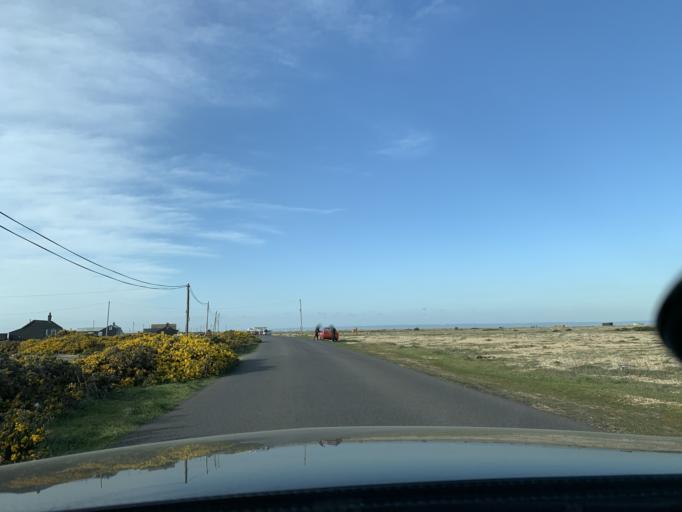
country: GB
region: England
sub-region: Kent
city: New Romney
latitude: 50.9203
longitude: 0.9767
